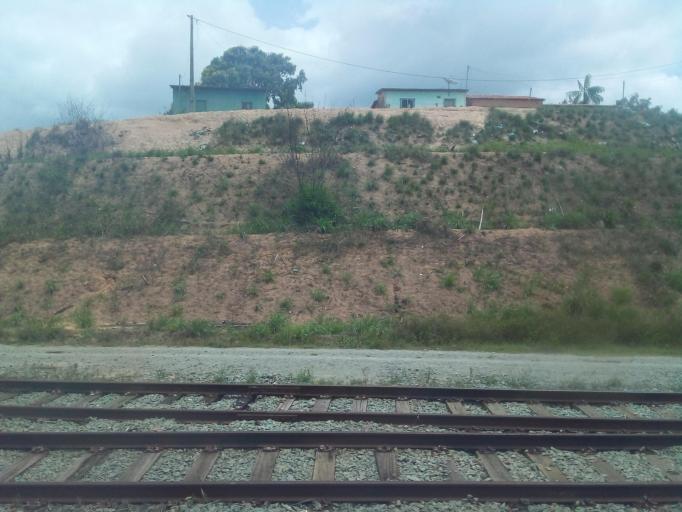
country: BR
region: Maranhao
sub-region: Santa Ines
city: Santa Ines
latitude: -3.6701
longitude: -45.8443
